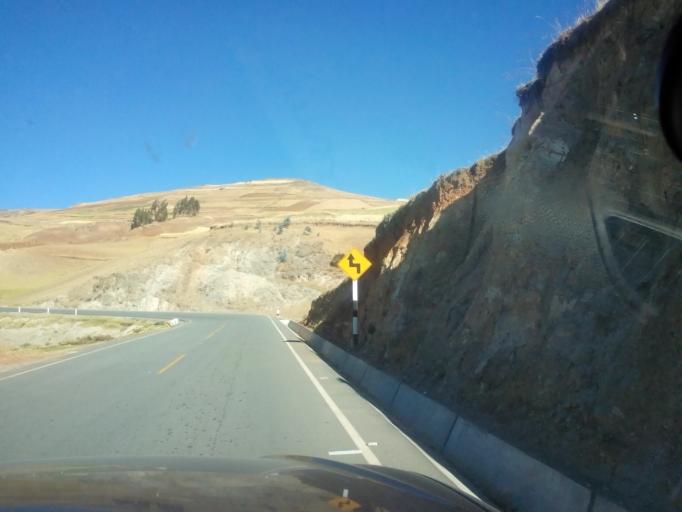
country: PE
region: Apurimac
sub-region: Provincia de Andahuaylas
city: Pacucha
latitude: -13.6608
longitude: -73.2888
